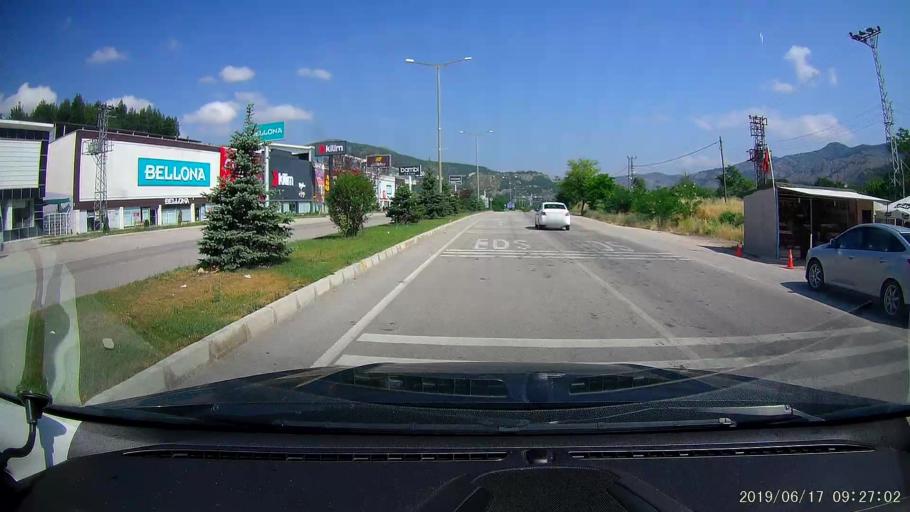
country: TR
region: Amasya
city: Amasya
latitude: 40.6732
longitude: 35.8297
